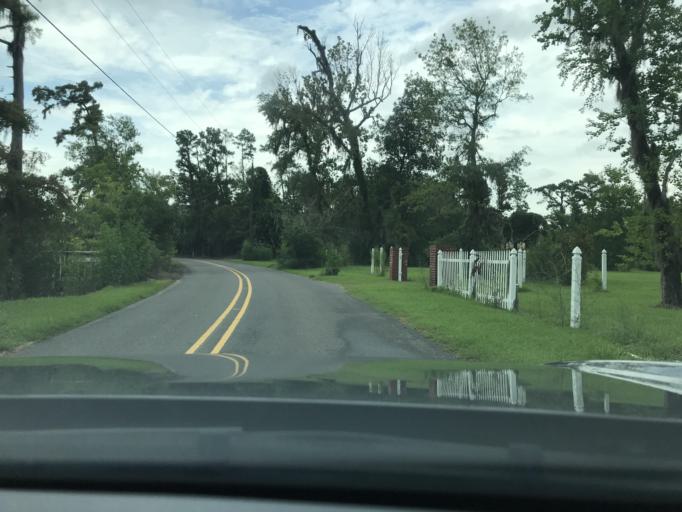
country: US
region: Louisiana
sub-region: Calcasieu Parish
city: Westlake
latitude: 30.2796
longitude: -93.2291
